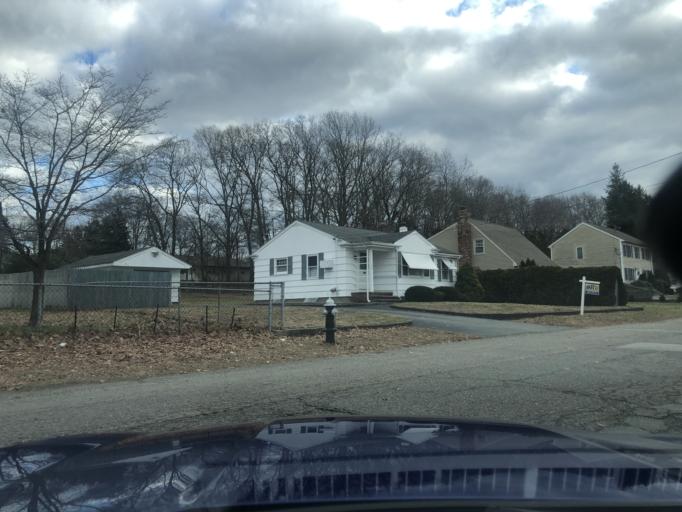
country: US
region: Massachusetts
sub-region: Plymouth County
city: Brockton
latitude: 42.1065
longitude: -71.0094
